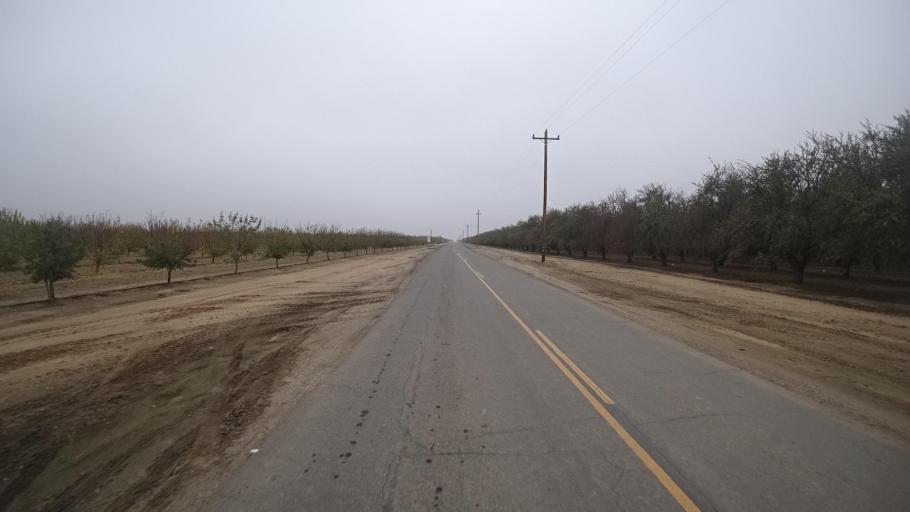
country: US
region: California
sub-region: Kern County
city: Wasco
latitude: 35.6004
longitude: -119.5091
